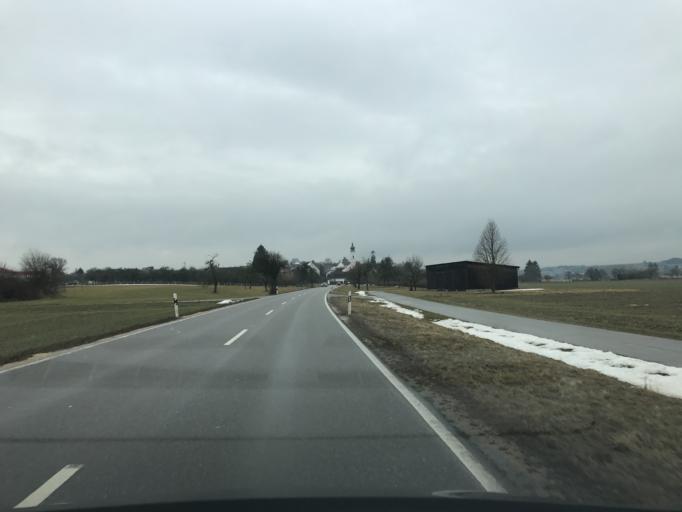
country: DE
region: Baden-Wuerttemberg
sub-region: Tuebingen Region
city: Griesingen
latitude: 48.2677
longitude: 9.7921
